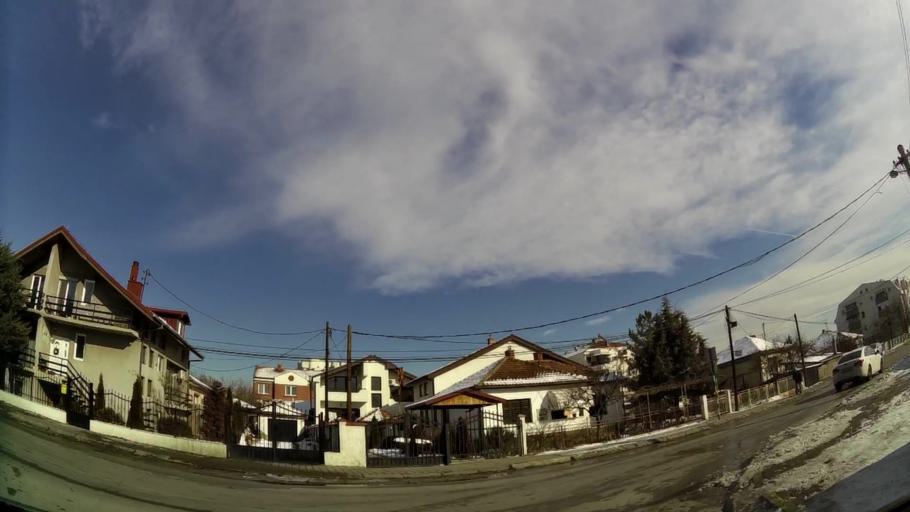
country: MK
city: Krushopek
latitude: 42.0056
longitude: 21.3664
